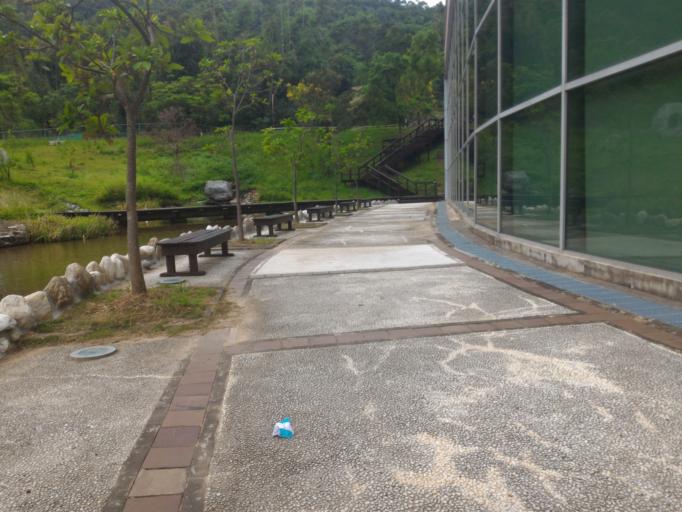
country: TW
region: Taipei
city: Taipei
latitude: 25.0405
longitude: 121.6116
